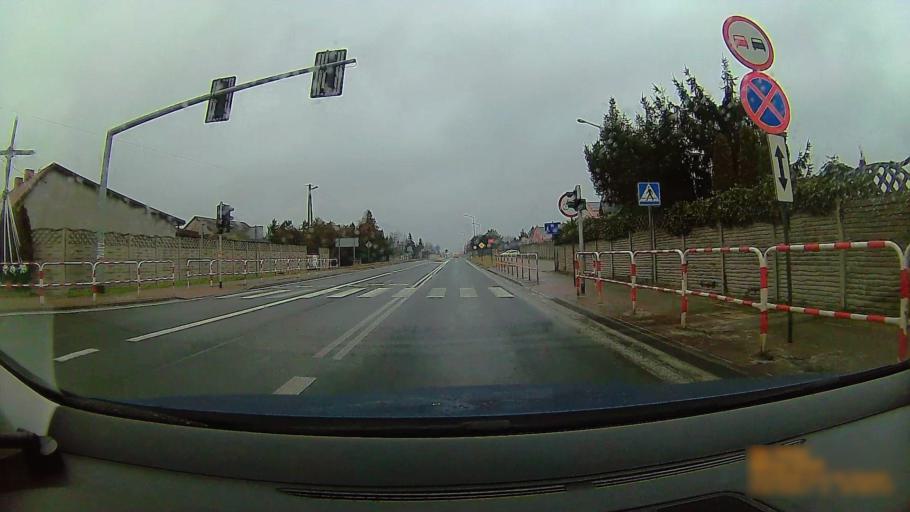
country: PL
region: Greater Poland Voivodeship
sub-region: Konin
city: Konin
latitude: 52.1763
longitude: 18.2716
